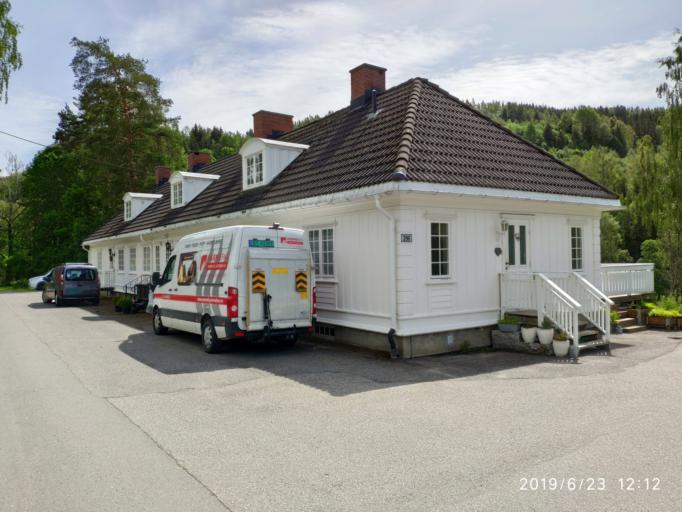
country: NO
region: Oppland
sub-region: Jevnaker
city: Jevnaker
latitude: 60.2004
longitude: 10.3338
